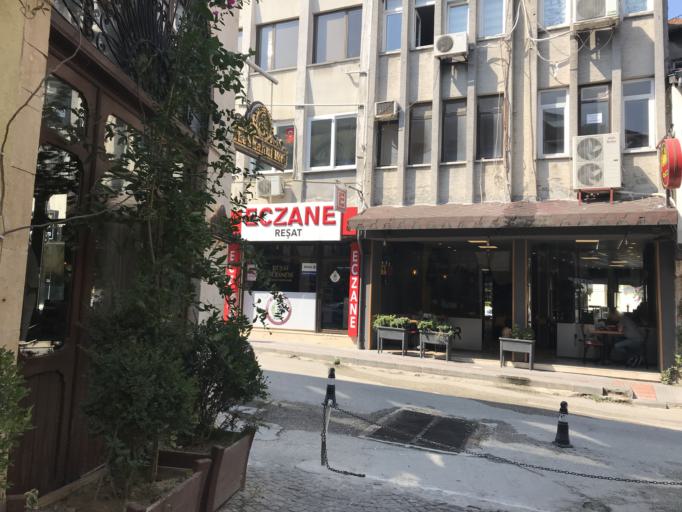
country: TR
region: Hatay
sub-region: Antakya Ilcesi
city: Antakya
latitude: 36.1992
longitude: 36.1609
